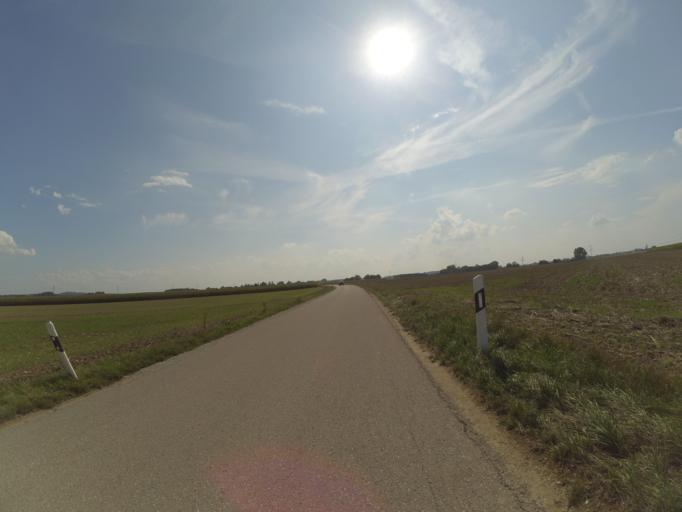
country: DE
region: Bavaria
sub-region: Swabia
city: Lamerdingen
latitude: 48.0974
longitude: 10.7708
